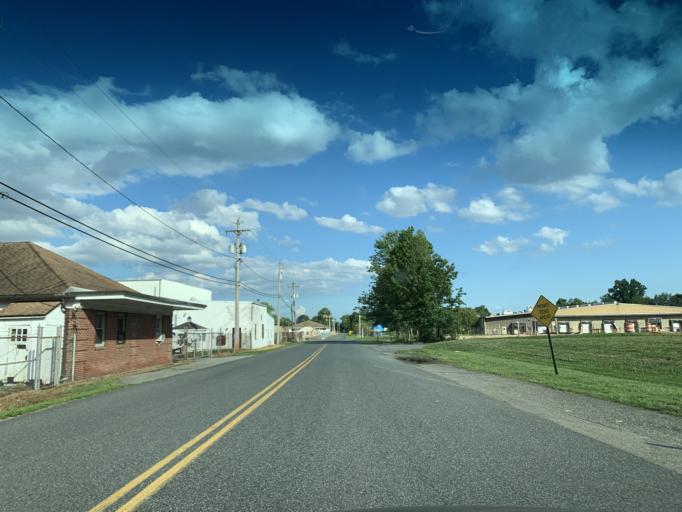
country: US
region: Maryland
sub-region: Harford County
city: Havre de Grace
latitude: 39.5332
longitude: -76.1073
